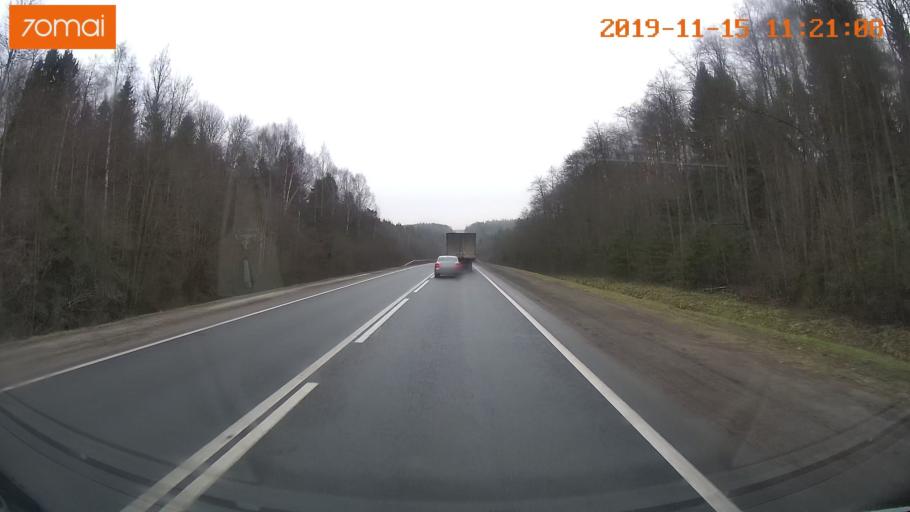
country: RU
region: Vologda
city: Molochnoye
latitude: 59.1435
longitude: 39.3302
